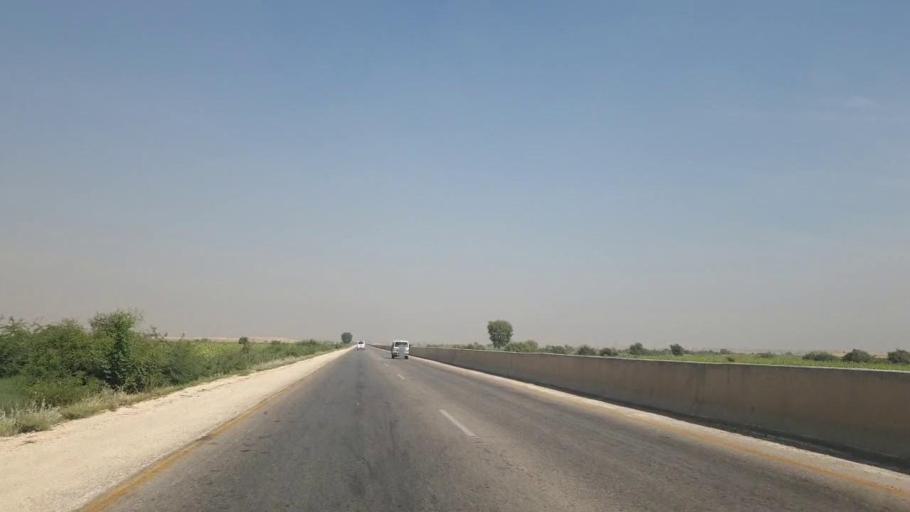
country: PK
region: Sindh
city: Jamshoro
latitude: 25.5469
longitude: 68.2939
